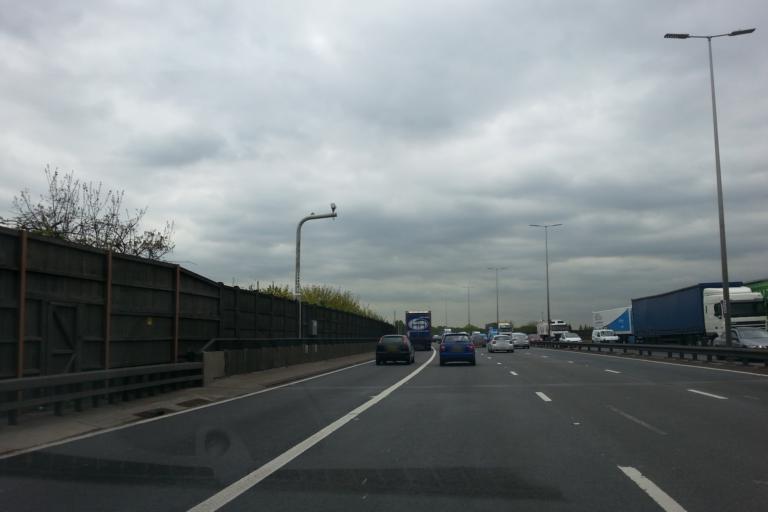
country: GB
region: England
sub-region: City and Borough of Birmingham
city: Hockley
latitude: 52.5393
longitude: -1.9101
